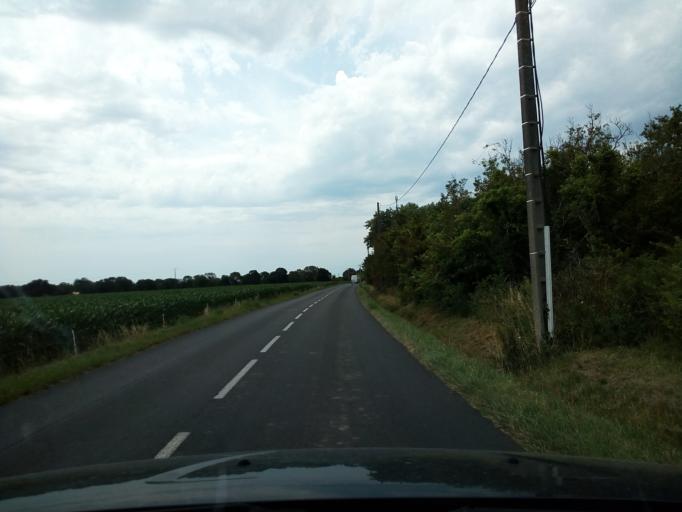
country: FR
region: Poitou-Charentes
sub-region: Departement de la Charente-Maritime
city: Dolus-d'Oleron
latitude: 45.9345
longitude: -1.3129
